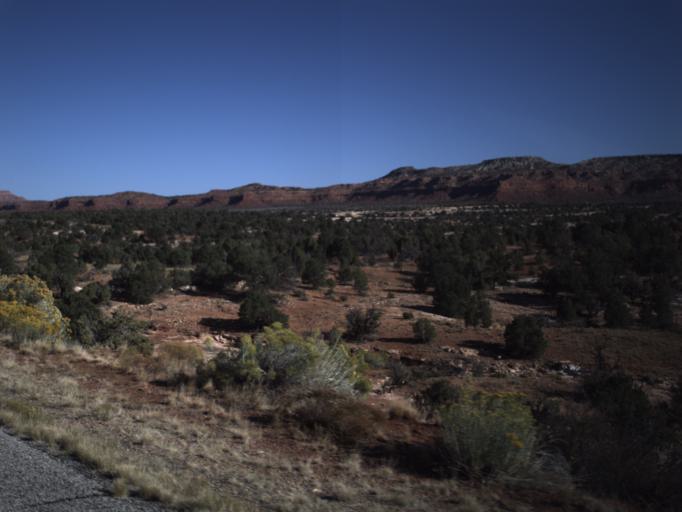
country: US
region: Utah
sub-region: San Juan County
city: Blanding
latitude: 37.6396
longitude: -110.1616
